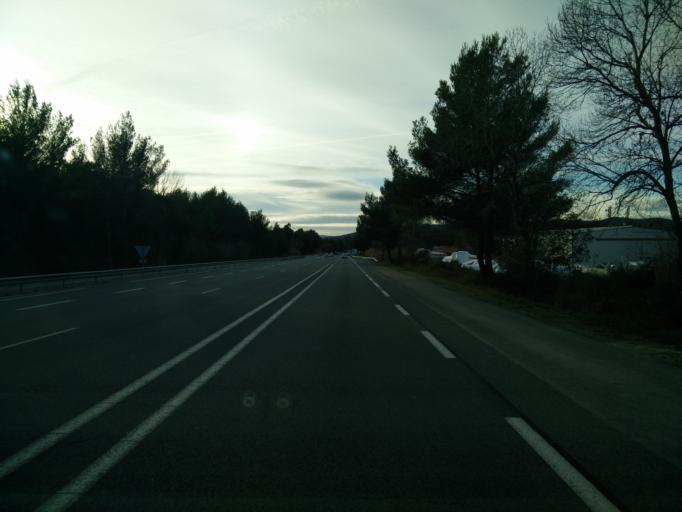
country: FR
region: Provence-Alpes-Cote d'Azur
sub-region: Departement du Var
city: La Londe-les-Maures
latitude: 43.1474
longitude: 6.2621
